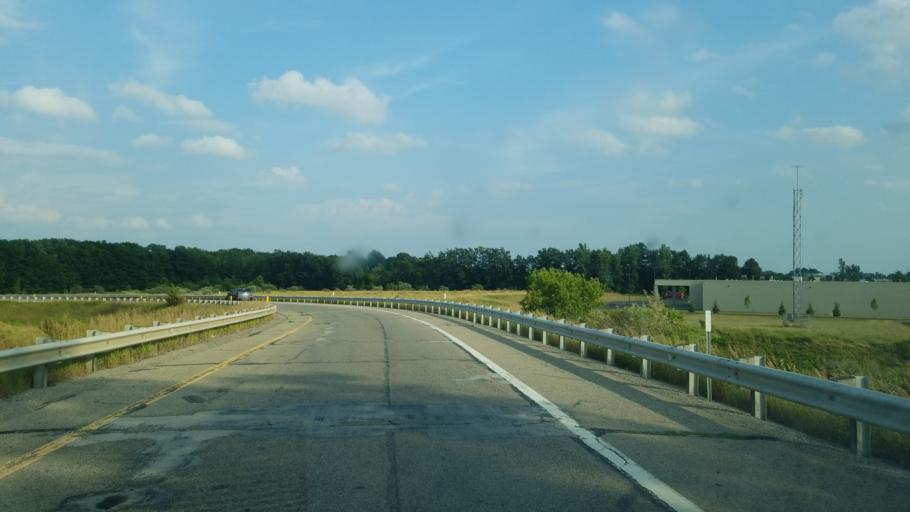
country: US
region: Michigan
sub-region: Gratiot County
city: Alma
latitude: 43.4069
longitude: -84.6631
